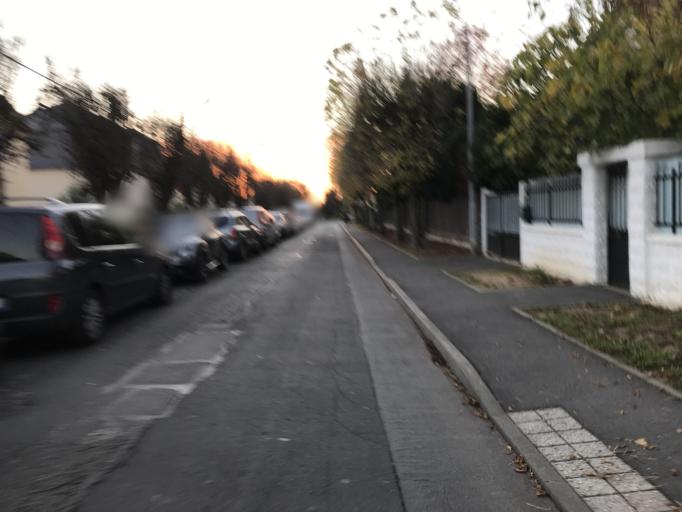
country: FR
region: Ile-de-France
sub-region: Departement de l'Essonne
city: Athis-Mons
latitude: 48.7101
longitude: 2.3806
